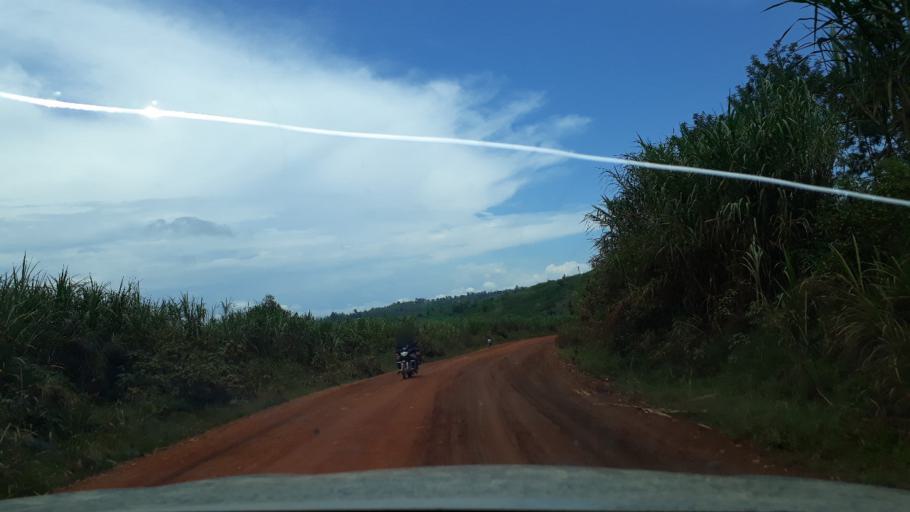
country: CD
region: Eastern Province
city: Bunia
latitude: 1.7092
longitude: 30.2908
